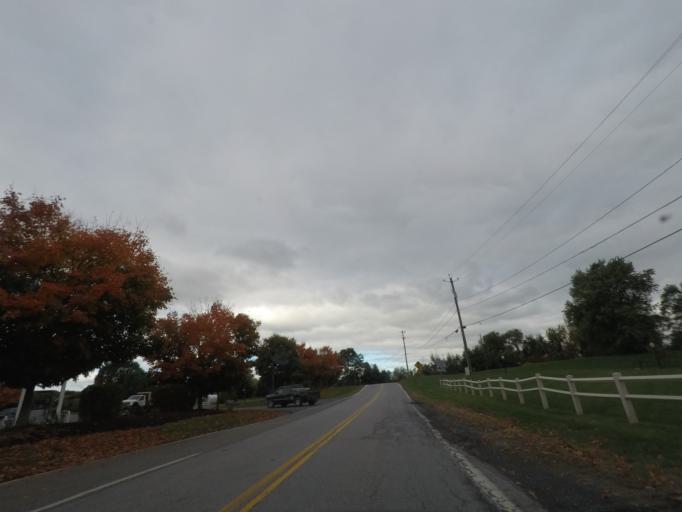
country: US
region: New York
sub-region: Saratoga County
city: Mechanicville
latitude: 42.8798
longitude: -73.7226
